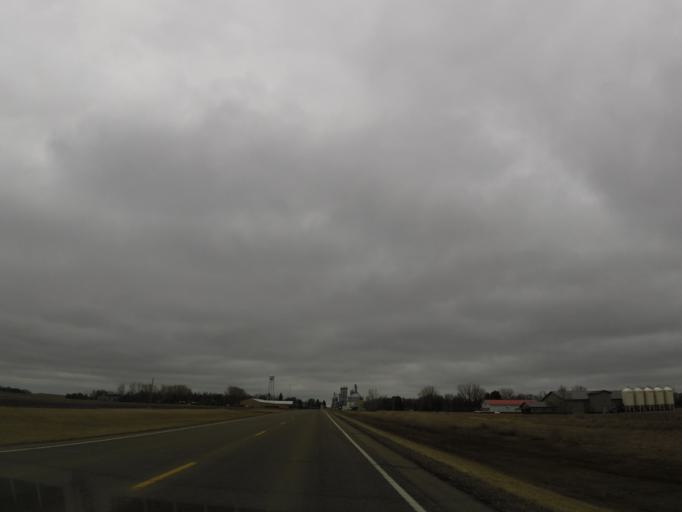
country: US
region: North Dakota
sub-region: Traill County
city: Hillsboro
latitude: 47.1990
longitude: -97.2176
